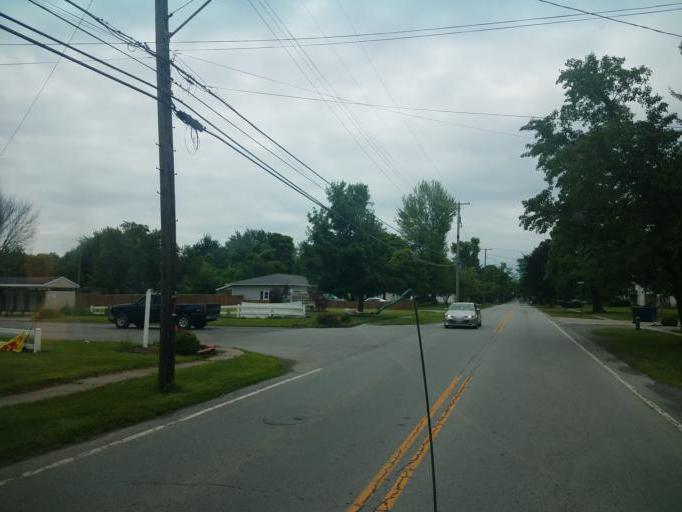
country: US
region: Ohio
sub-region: Hardin County
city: Ada
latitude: 40.7796
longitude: -83.8232
